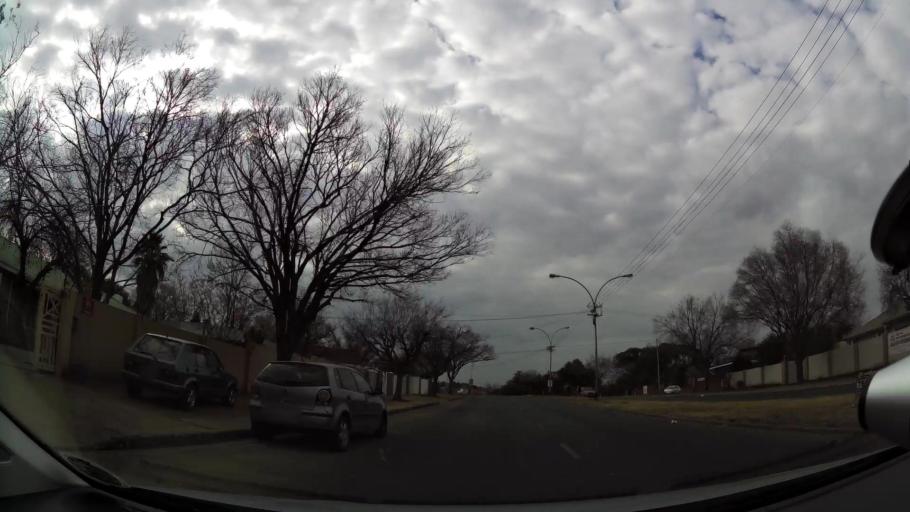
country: ZA
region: Orange Free State
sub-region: Mangaung Metropolitan Municipality
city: Bloemfontein
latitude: -29.0861
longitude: 26.2161
